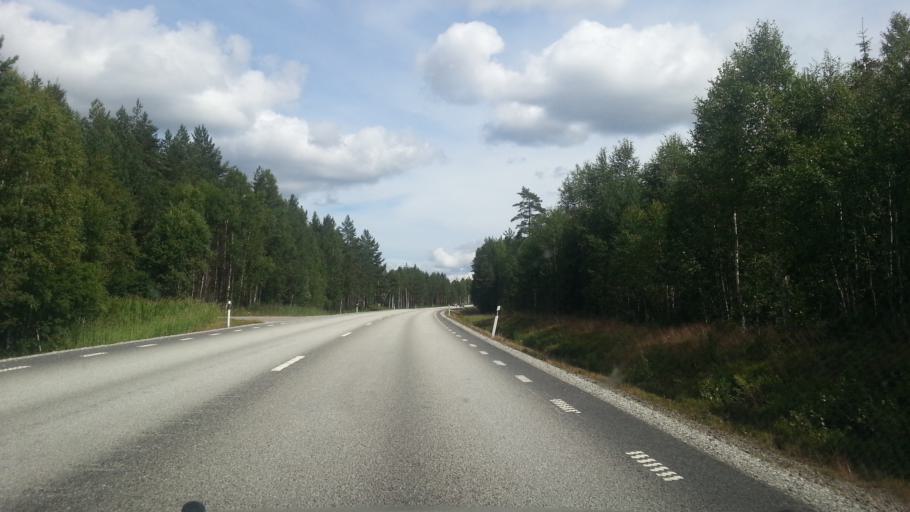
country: SE
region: Vaestmanland
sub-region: Skinnskattebergs Kommun
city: Skinnskatteberg
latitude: 59.7582
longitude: 15.4607
